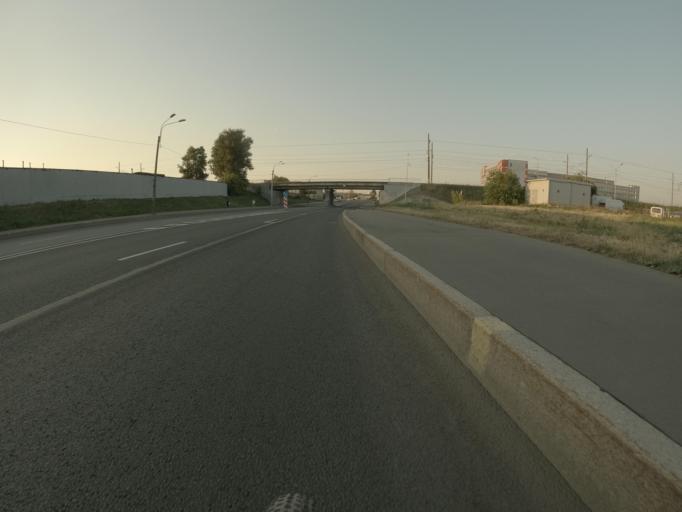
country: RU
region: St.-Petersburg
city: Avtovo
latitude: 59.8595
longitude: 30.2840
